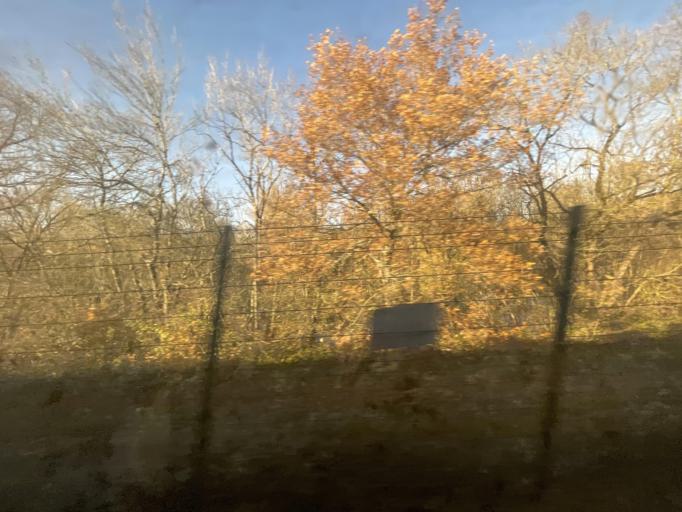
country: FR
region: Pays de la Loire
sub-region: Departement de la Loire-Atlantique
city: Thouare-sur-Loire
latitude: 47.2791
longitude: -1.4182
